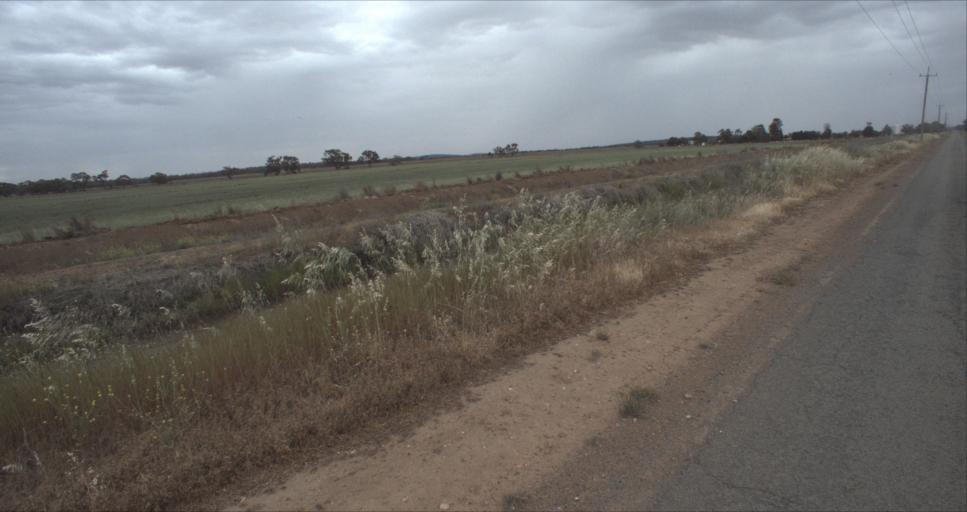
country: AU
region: New South Wales
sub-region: Leeton
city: Leeton
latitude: -34.4267
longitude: 146.3374
